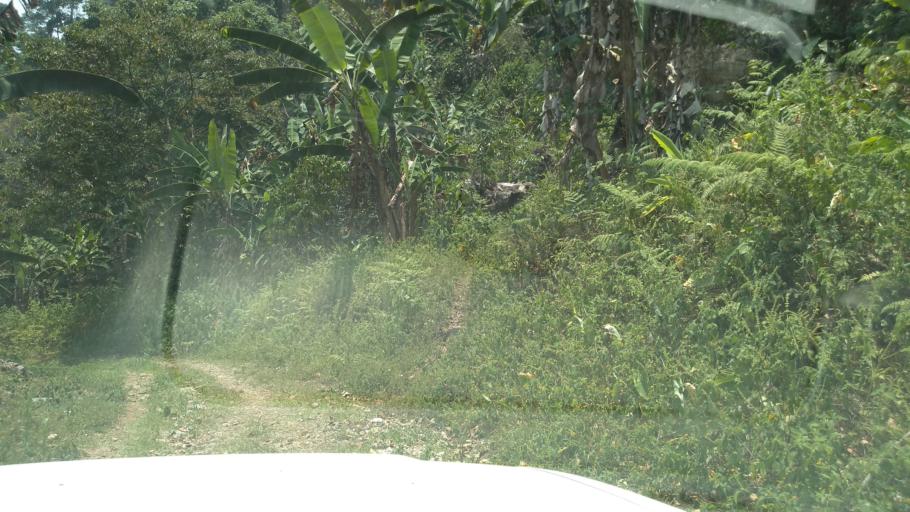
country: MX
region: Veracruz
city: Motzorongo
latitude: 18.6067
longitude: -96.7617
